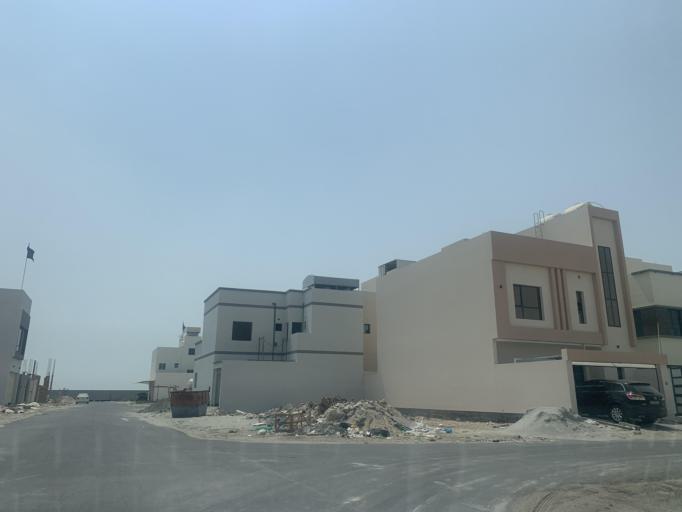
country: BH
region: Central Governorate
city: Madinat Hamad
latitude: 26.1279
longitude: 50.4690
